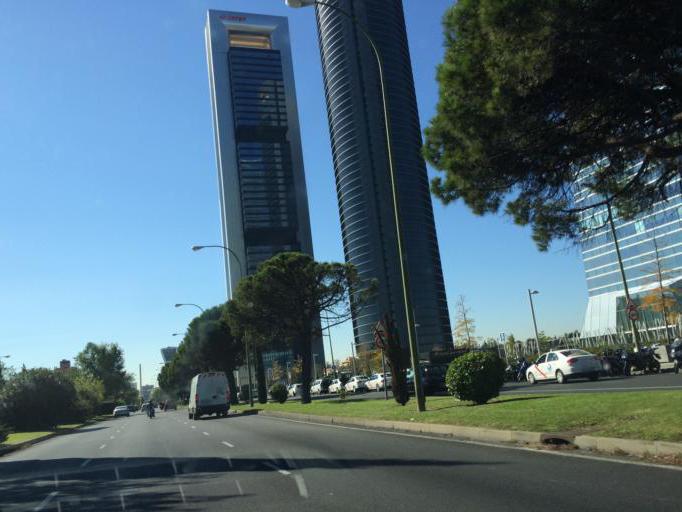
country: ES
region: Madrid
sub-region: Provincia de Madrid
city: Pinar de Chamartin
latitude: 40.4789
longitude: -3.6860
